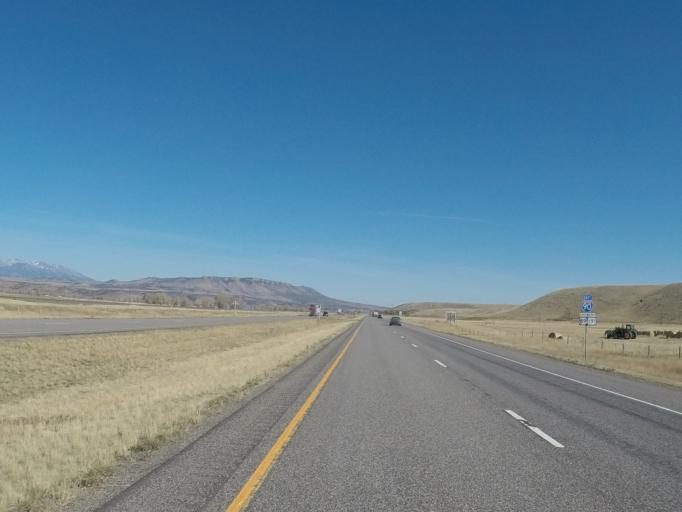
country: US
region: Montana
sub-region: Park County
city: Livingston
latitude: 45.6920
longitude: -110.4921
